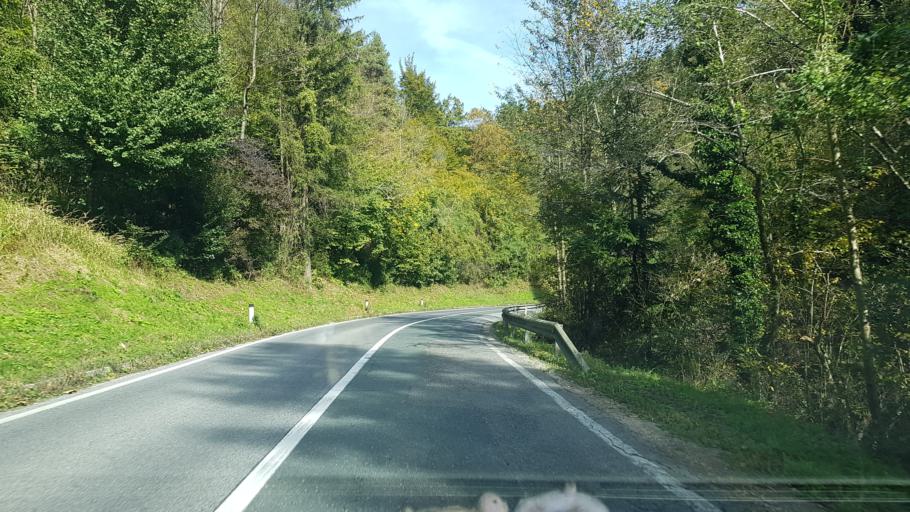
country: SI
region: Velenje
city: Velenje
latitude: 46.4026
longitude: 15.1783
